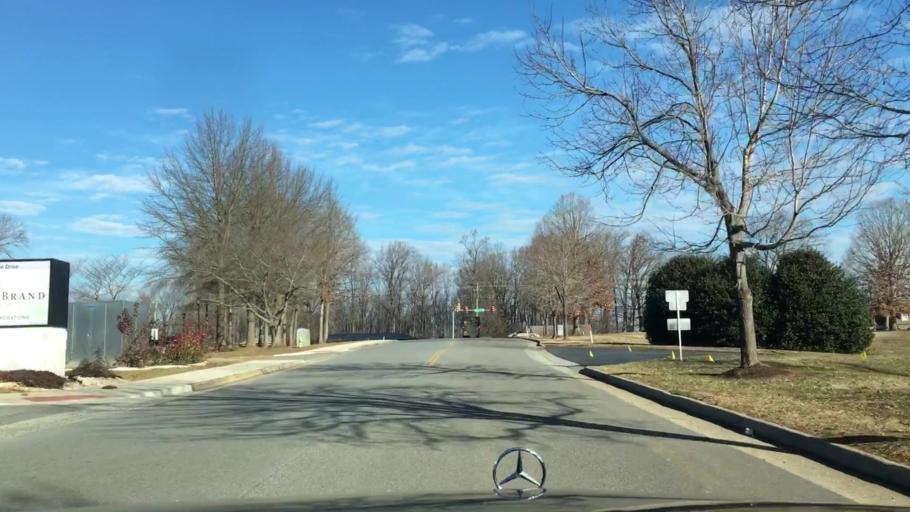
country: US
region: Virginia
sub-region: Bedford County
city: Forest
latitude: 37.3757
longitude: -79.2400
